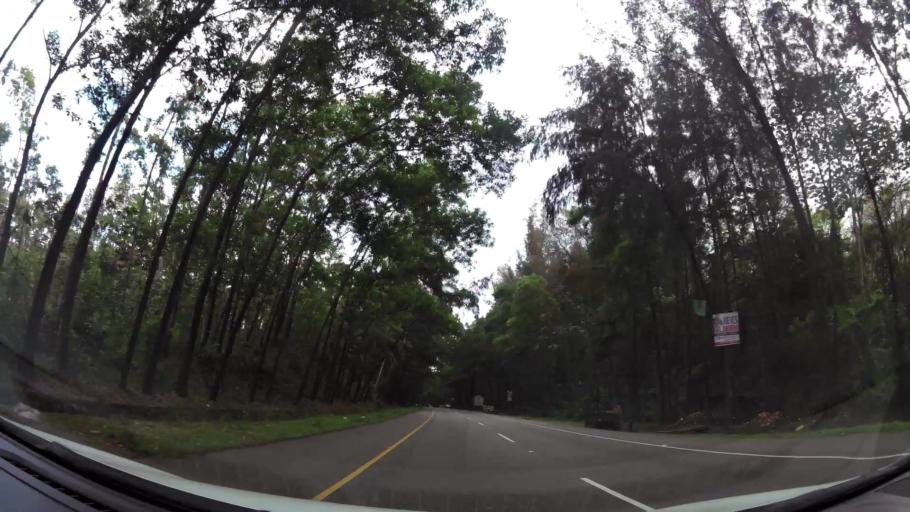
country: DO
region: La Vega
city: Rincon
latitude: 19.1245
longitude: -70.4532
